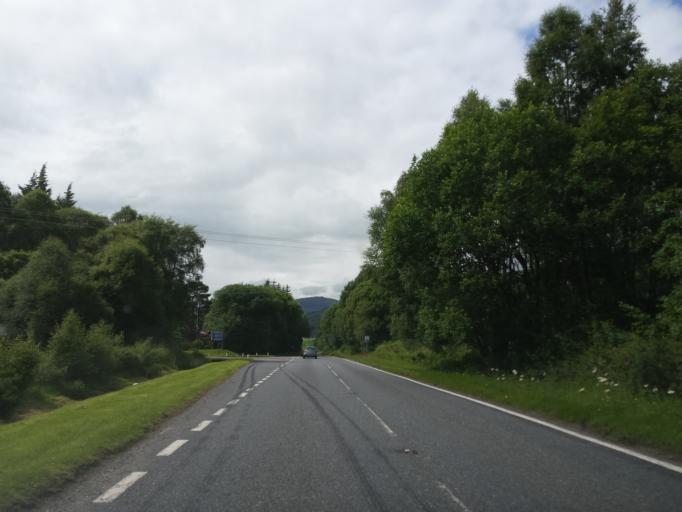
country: GB
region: Scotland
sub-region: Highland
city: Fort William
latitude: 56.8475
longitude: -5.1593
